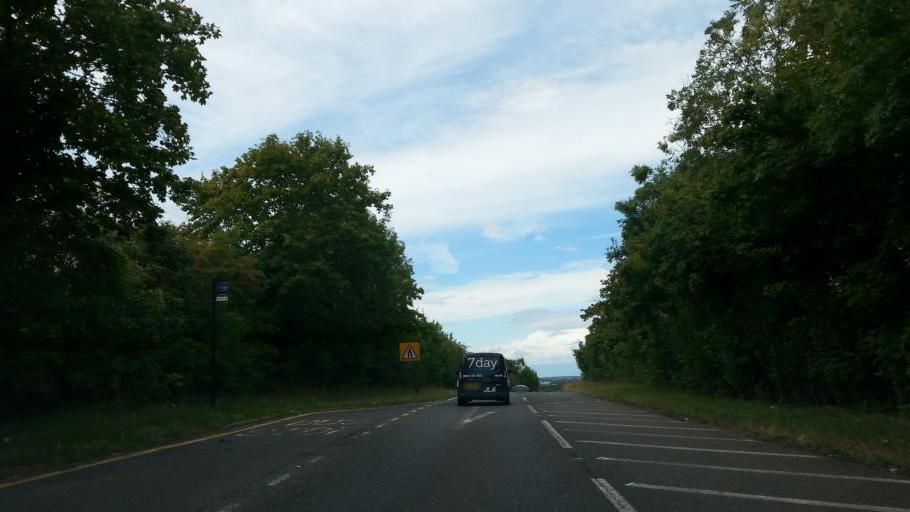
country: GB
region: England
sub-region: Cambridgeshire
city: Sawston
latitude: 52.1576
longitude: 0.1774
